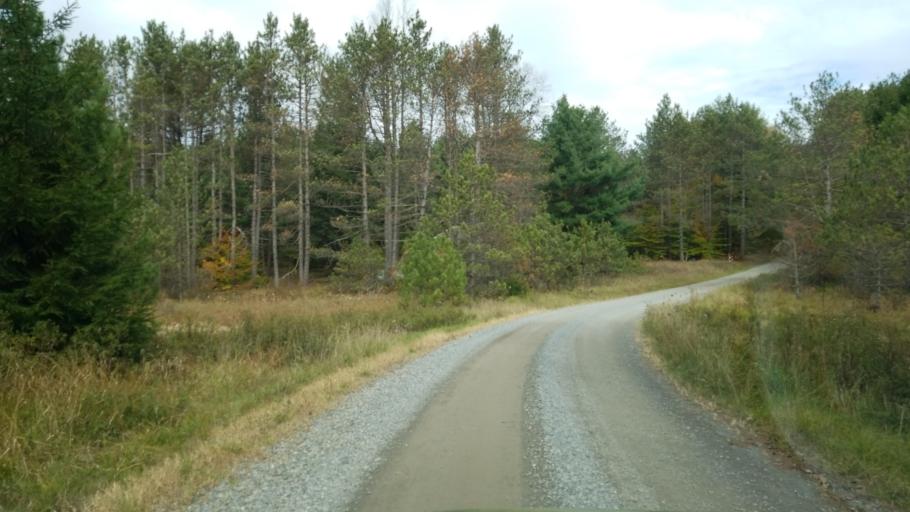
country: US
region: Pennsylvania
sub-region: Clearfield County
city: Clearfield
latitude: 41.2030
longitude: -78.4240
